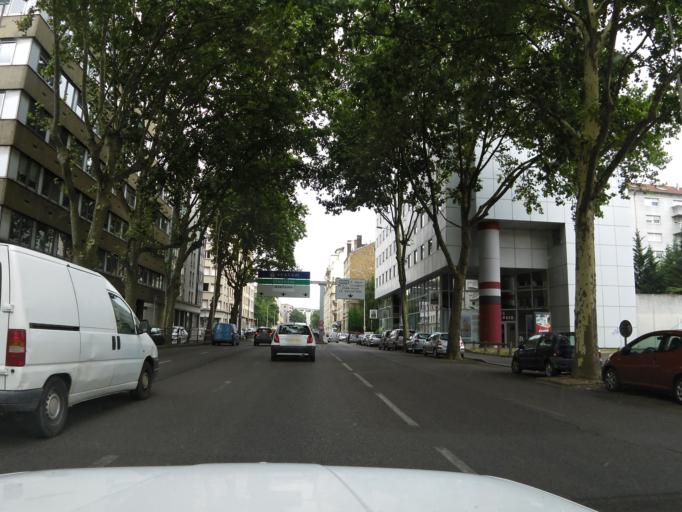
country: FR
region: Rhone-Alpes
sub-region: Departement du Rhone
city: Lyon
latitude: 45.7546
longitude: 4.8531
